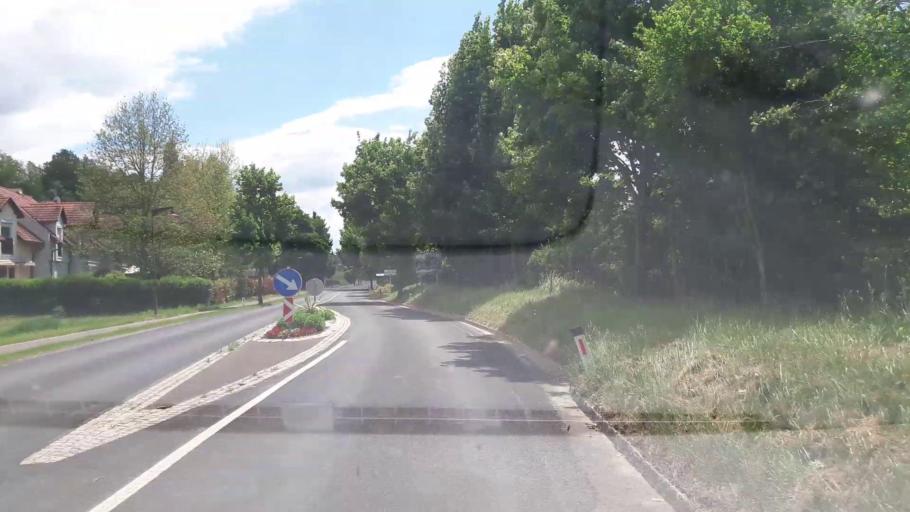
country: AT
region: Styria
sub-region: Politischer Bezirk Suedoststeiermark
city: Unterlamm
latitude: 46.9827
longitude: 16.0552
